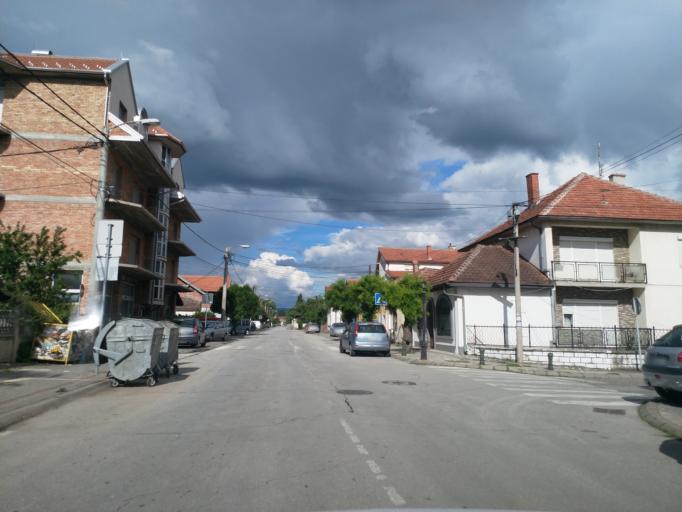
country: RS
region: Central Serbia
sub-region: Pomoravski Okrug
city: Paracin
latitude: 43.8570
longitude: 21.4128
